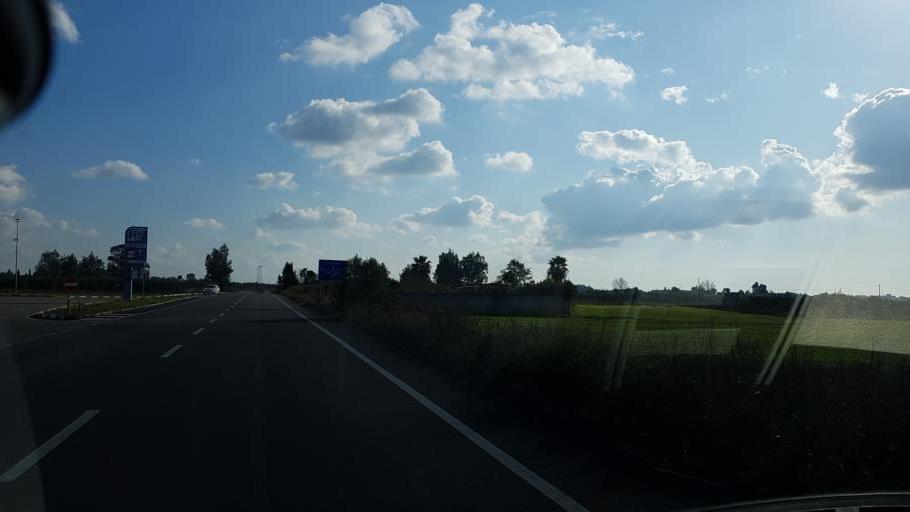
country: IT
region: Apulia
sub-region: Provincia di Lecce
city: Veglie
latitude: 40.3417
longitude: 17.9783
